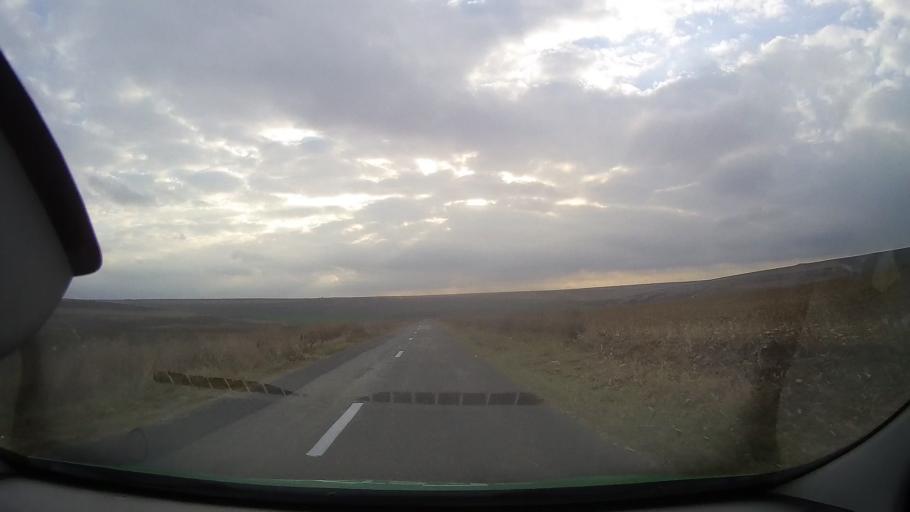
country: RO
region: Constanta
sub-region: Comuna Deleni
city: Pietreni
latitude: 44.1184
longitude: 28.1023
